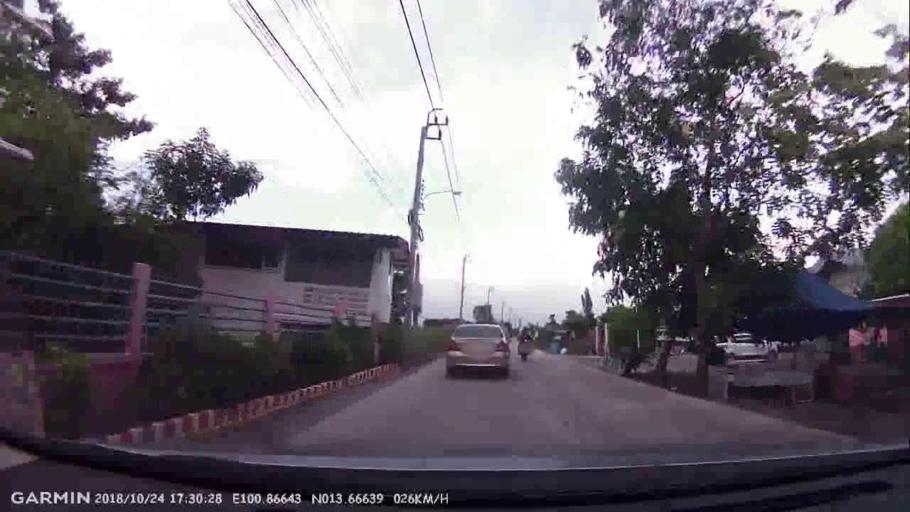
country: TH
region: Samut Prakan
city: Ban Khlong Bang Sao Thong
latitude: 13.6664
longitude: 100.8665
